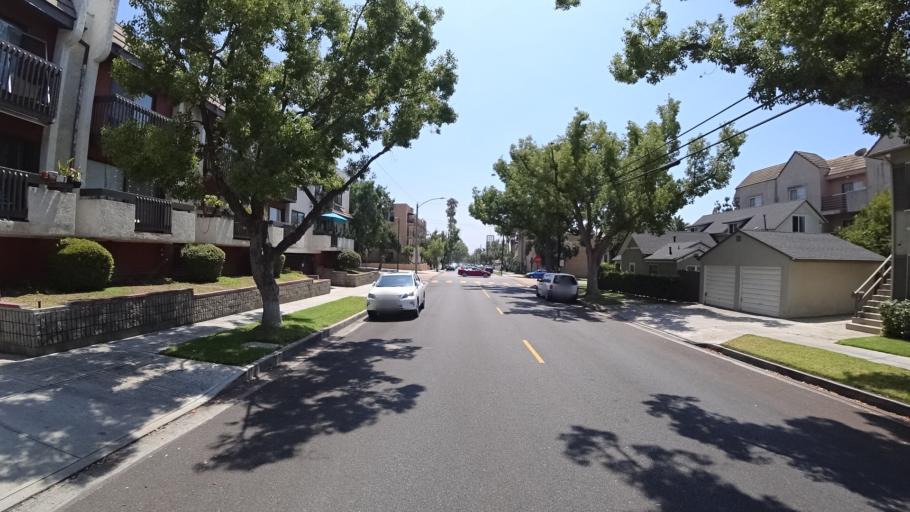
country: US
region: California
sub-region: Los Angeles County
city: Burbank
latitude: 34.1858
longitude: -118.3042
